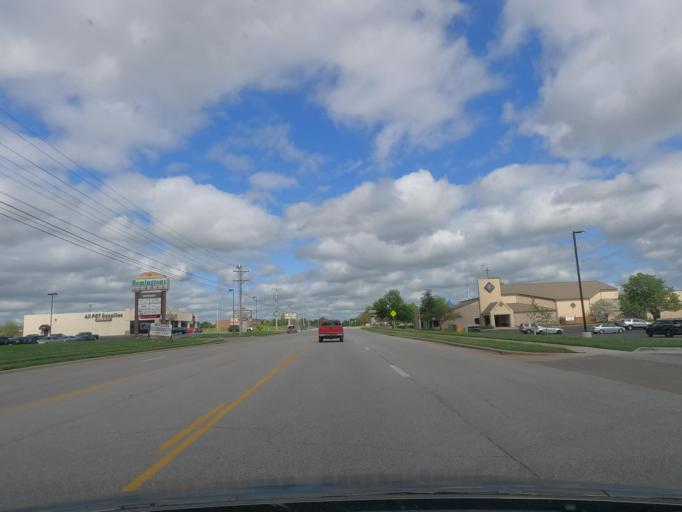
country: US
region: Missouri
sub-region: Greene County
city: Battlefield
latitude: 37.1383
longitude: -93.3162
